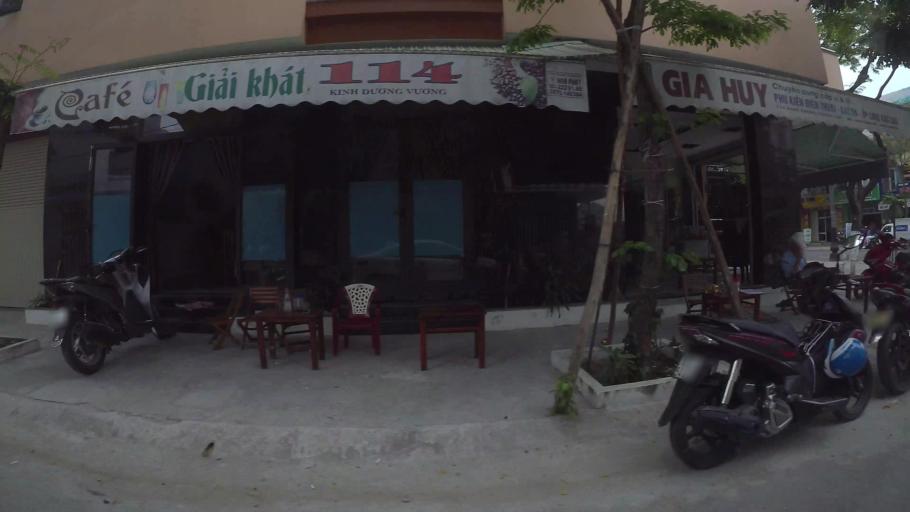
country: VN
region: Da Nang
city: Lien Chieu
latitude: 16.0737
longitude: 108.1713
